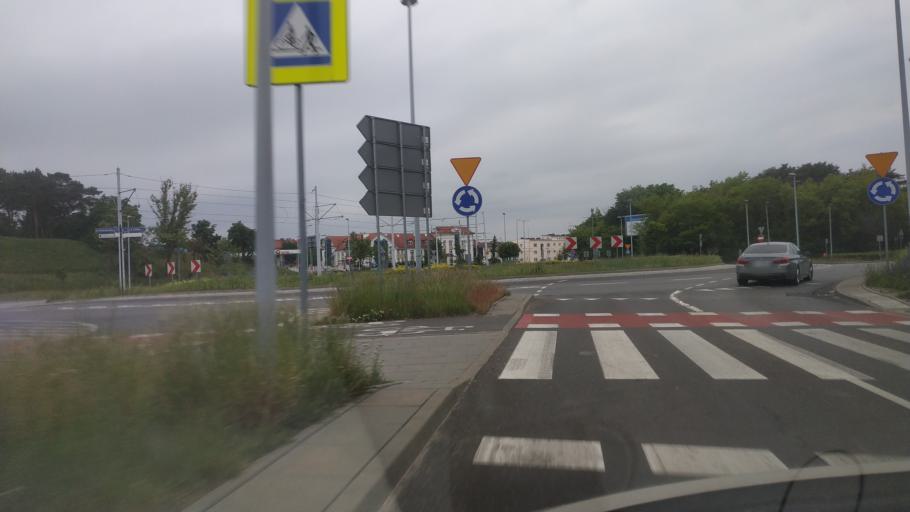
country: PL
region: Kujawsko-Pomorskie
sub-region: Torun
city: Torun
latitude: 53.0155
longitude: 18.5850
